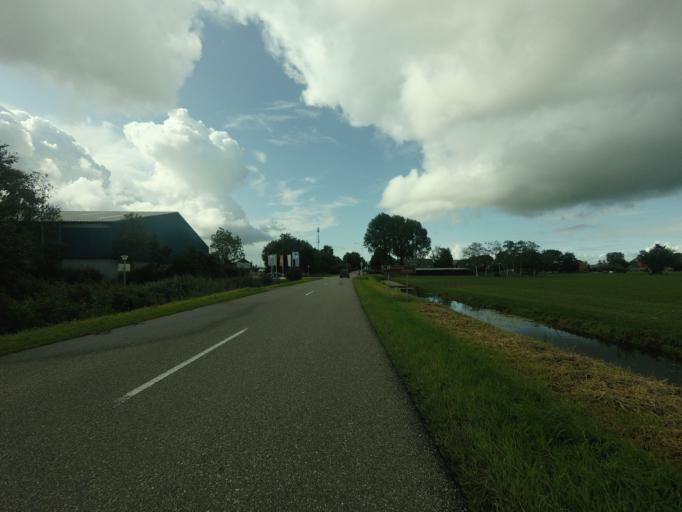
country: NL
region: Friesland
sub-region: Gemeente Boarnsterhim
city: Warten
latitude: 53.1518
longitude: 5.9060
